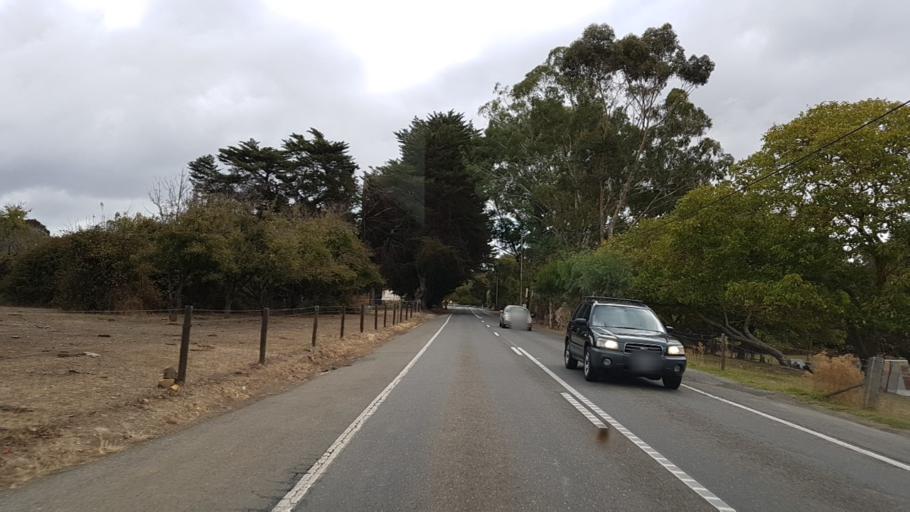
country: AU
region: South Australia
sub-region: Adelaide Hills
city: Gumeracha
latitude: -34.8405
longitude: 138.8284
